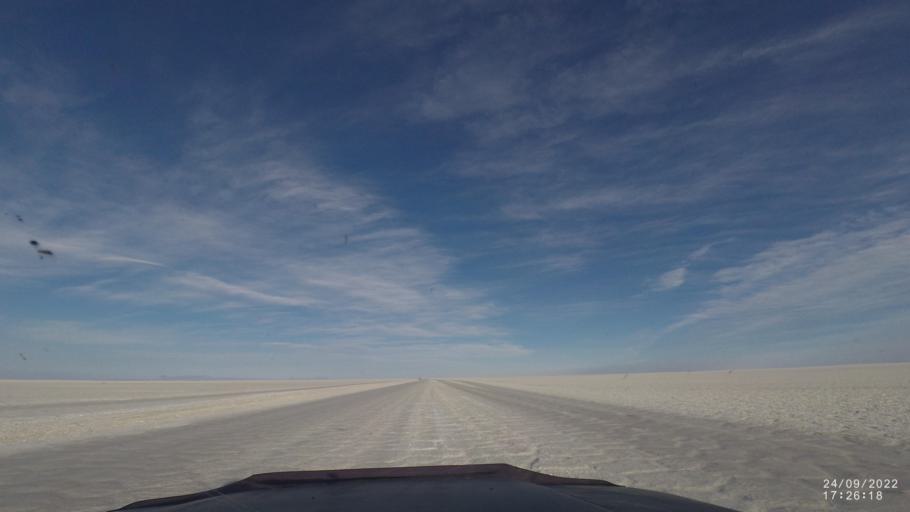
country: BO
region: Potosi
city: Colchani
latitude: -20.2939
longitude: -67.4711
